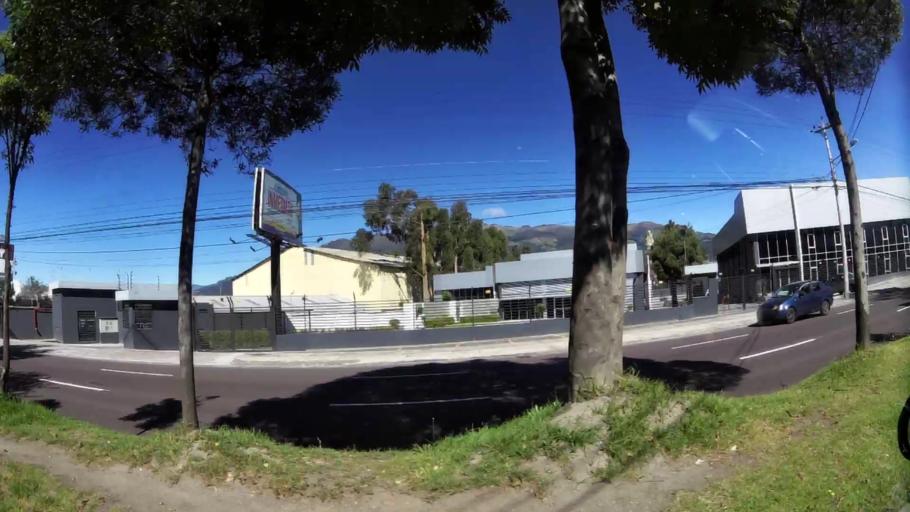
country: EC
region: Pichincha
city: Quito
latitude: -0.1279
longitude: -78.4772
